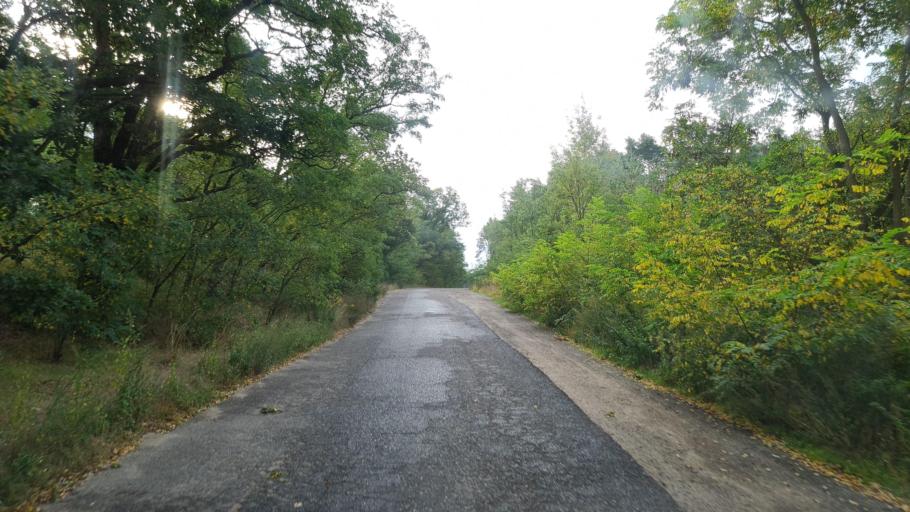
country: DE
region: Brandenburg
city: Kasel-Golzig
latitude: 51.9379
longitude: 13.7426
